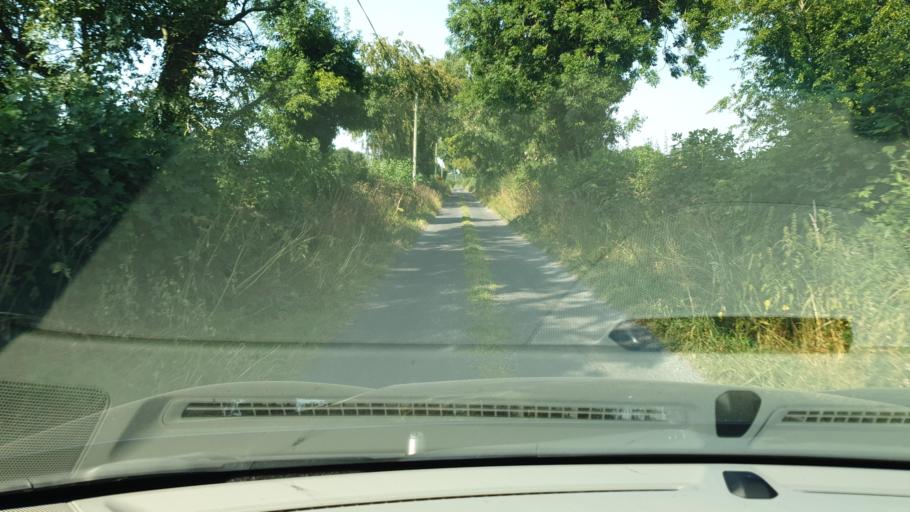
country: IE
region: Leinster
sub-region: An Mhi
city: Athboy
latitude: 53.6188
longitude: -6.9923
